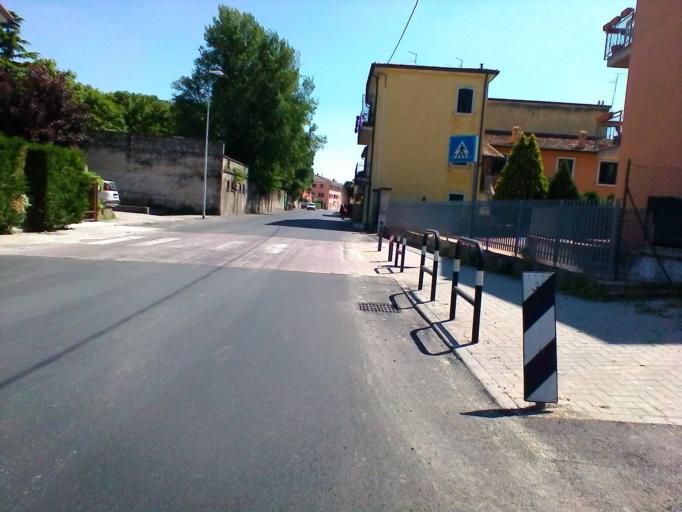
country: IT
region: Veneto
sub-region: Provincia di Verona
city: Povegliano Veronese
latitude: 45.3517
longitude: 10.8824
